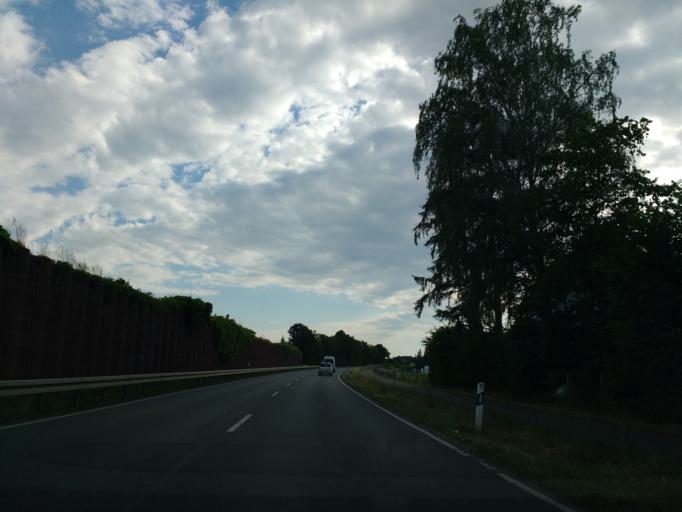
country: DE
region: North Rhine-Westphalia
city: Geseke
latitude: 51.6384
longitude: 8.5214
